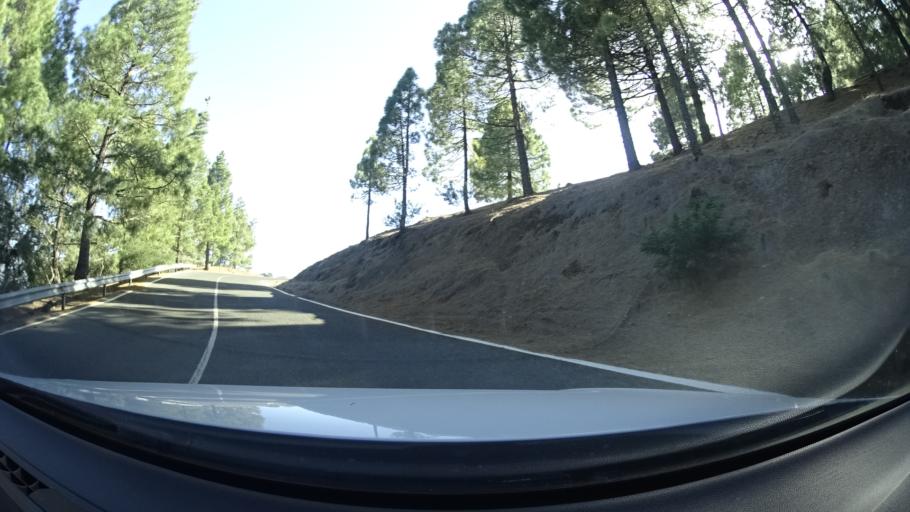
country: ES
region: Canary Islands
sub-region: Provincia de Las Palmas
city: Vega de San Mateo
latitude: 27.9634
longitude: -15.5379
